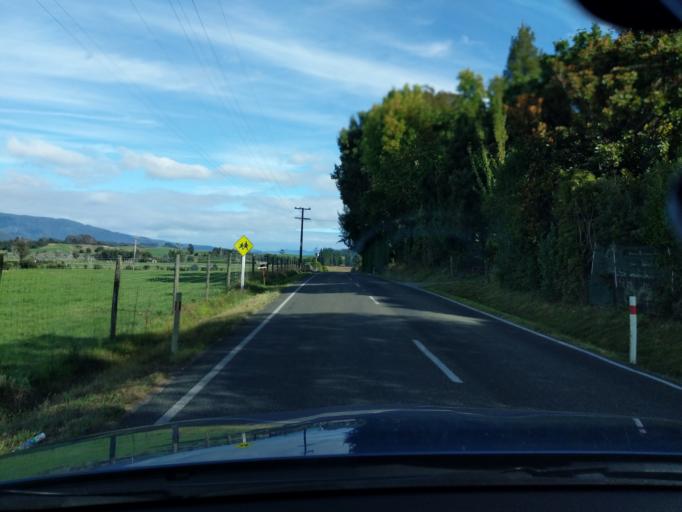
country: NZ
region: Tasman
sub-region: Tasman District
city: Takaka
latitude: -40.8509
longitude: 172.8425
